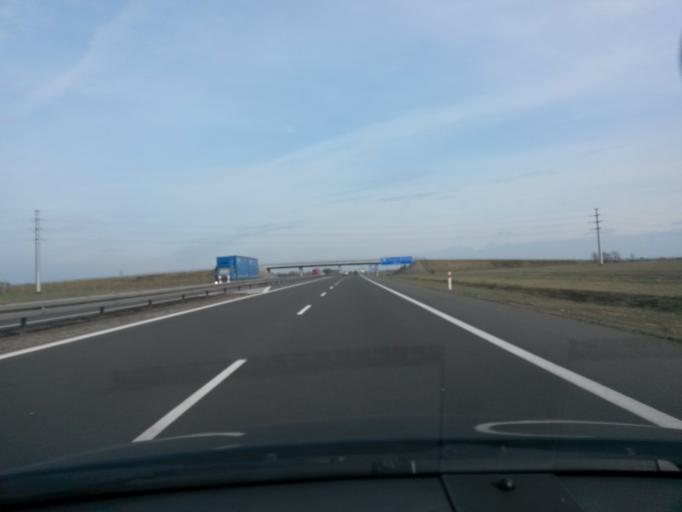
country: PL
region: Greater Poland Voivodeship
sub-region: Powiat poznanski
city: Swarzedz
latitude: 52.3324
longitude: 17.0756
